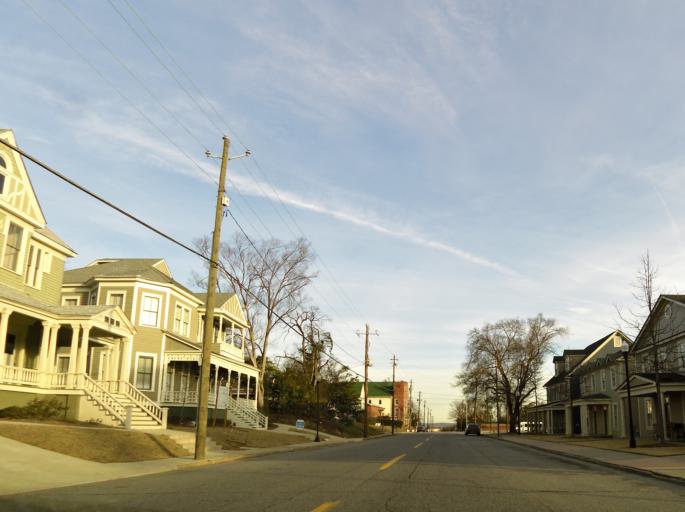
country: US
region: Georgia
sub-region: Bibb County
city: Macon
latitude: 32.8322
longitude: -83.6421
